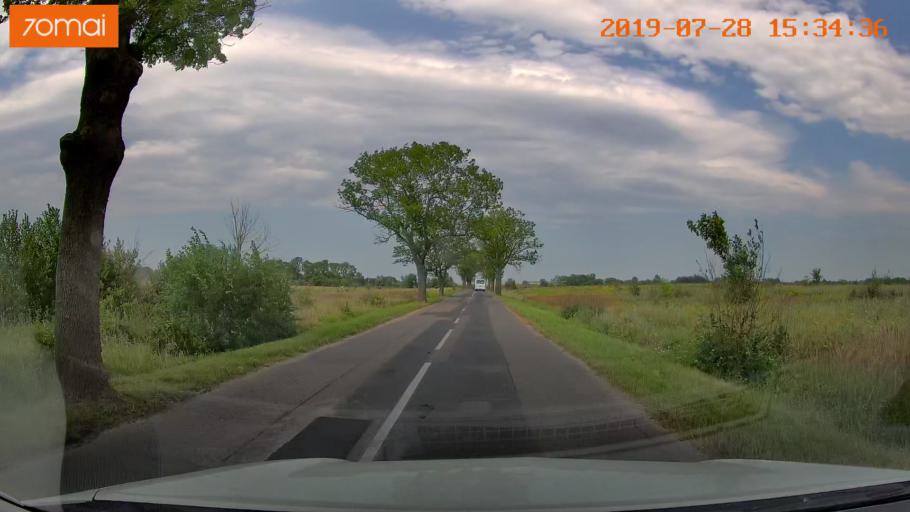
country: RU
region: Kaliningrad
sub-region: Gorod Kaliningrad
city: Yantarnyy
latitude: 54.8810
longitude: 19.9708
